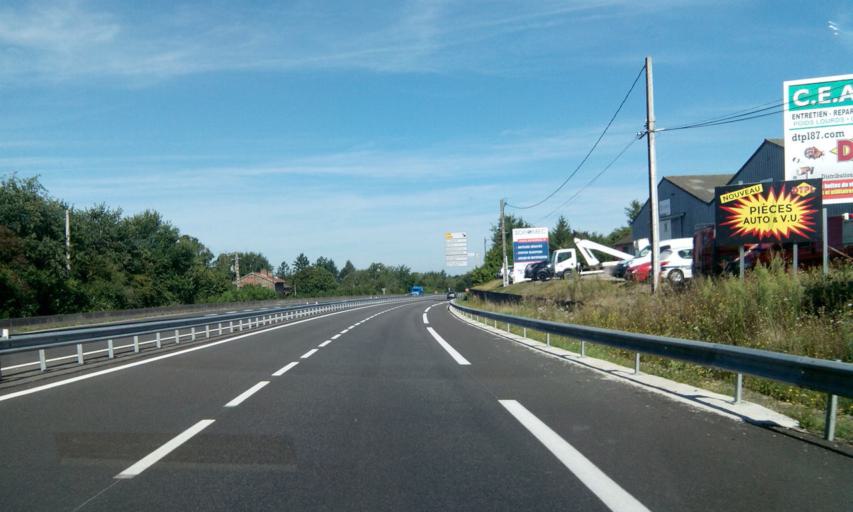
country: FR
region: Limousin
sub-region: Departement de la Haute-Vienne
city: Aixe-sur-Vienne
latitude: 45.8493
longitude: 1.1648
